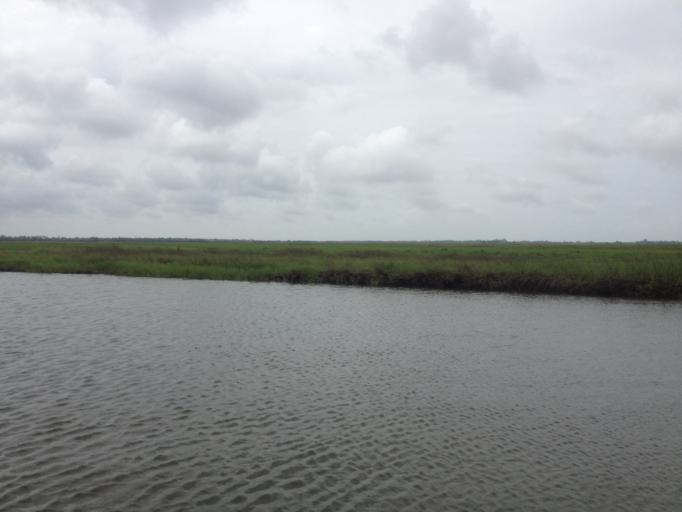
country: BJ
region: Mono
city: Come
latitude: 6.3696
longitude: 1.9430
